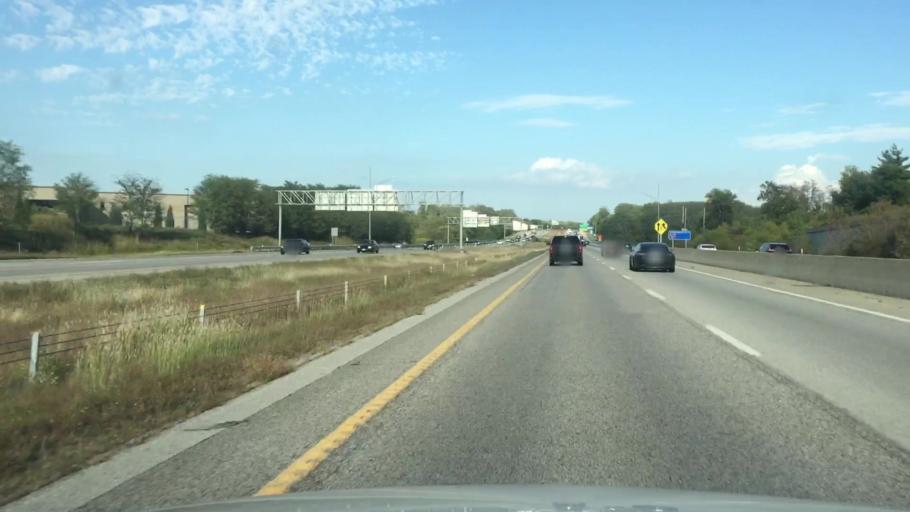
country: US
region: Missouri
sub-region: Jackson County
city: Lees Summit
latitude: 38.9374
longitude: -94.3993
